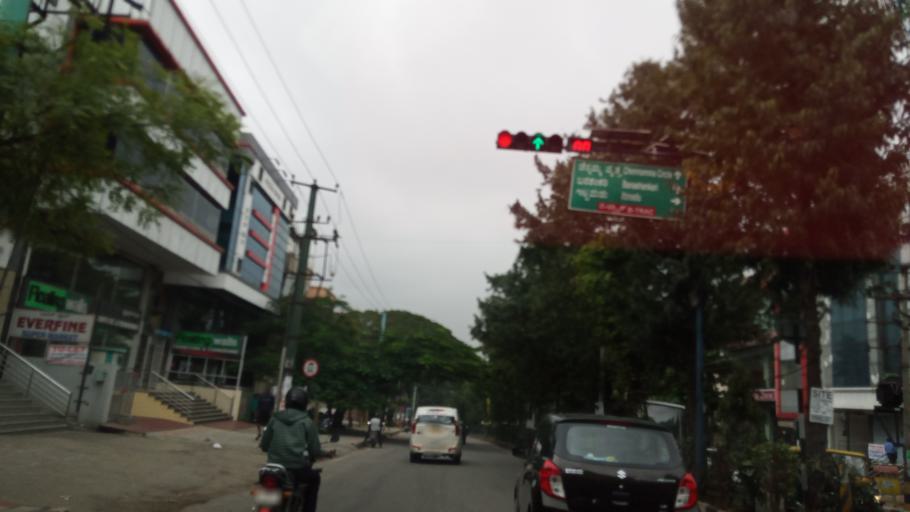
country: IN
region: Karnataka
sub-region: Bangalore Urban
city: Bangalore
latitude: 12.9281
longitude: 77.5462
